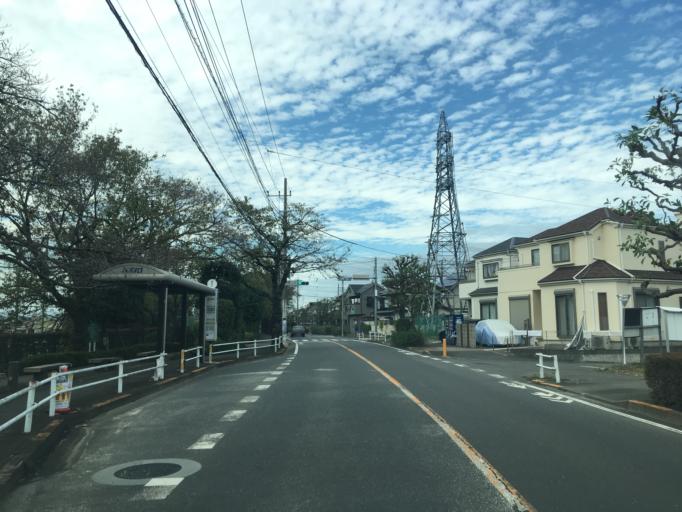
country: JP
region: Tokyo
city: Chofugaoka
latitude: 35.6408
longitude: 139.5471
